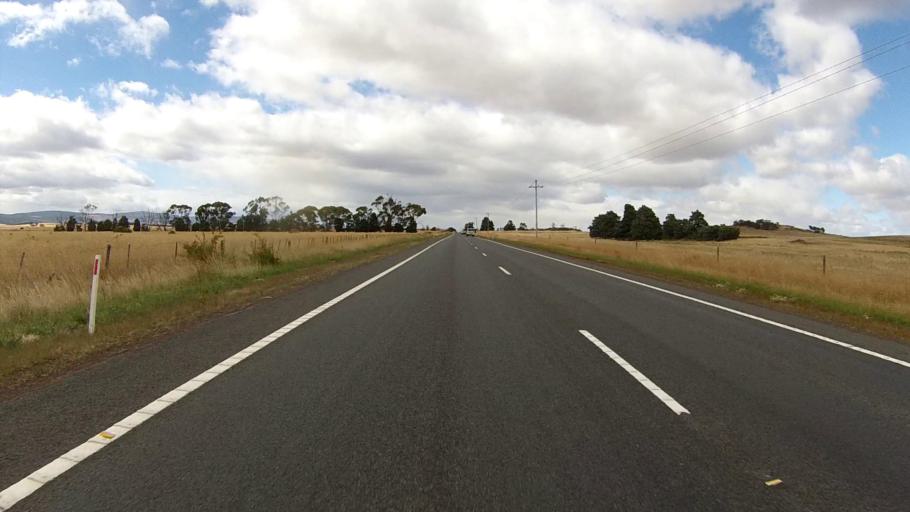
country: AU
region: Tasmania
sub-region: Northern Midlands
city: Evandale
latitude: -41.8931
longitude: 147.4719
